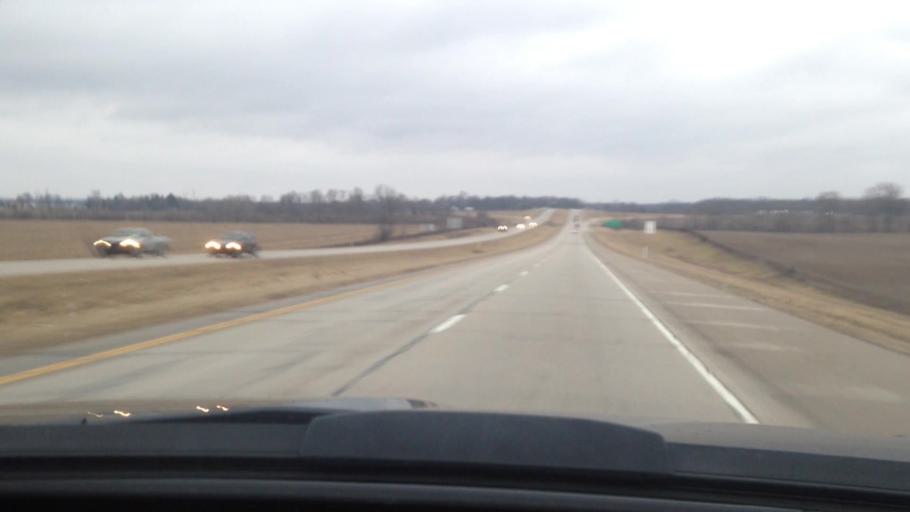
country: US
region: Indiana
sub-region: Delaware County
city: Muncie
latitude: 40.1883
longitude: -85.3365
